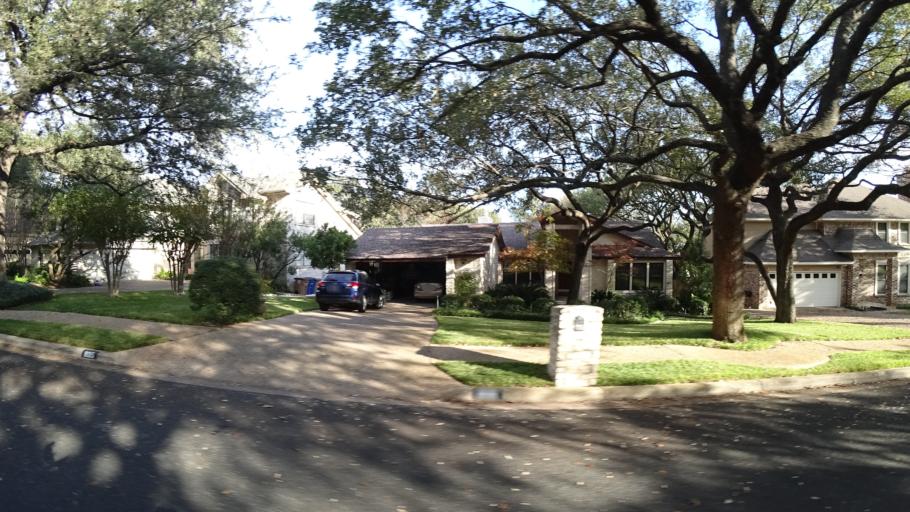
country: US
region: Texas
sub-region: Williamson County
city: Jollyville
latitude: 30.3683
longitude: -97.7509
